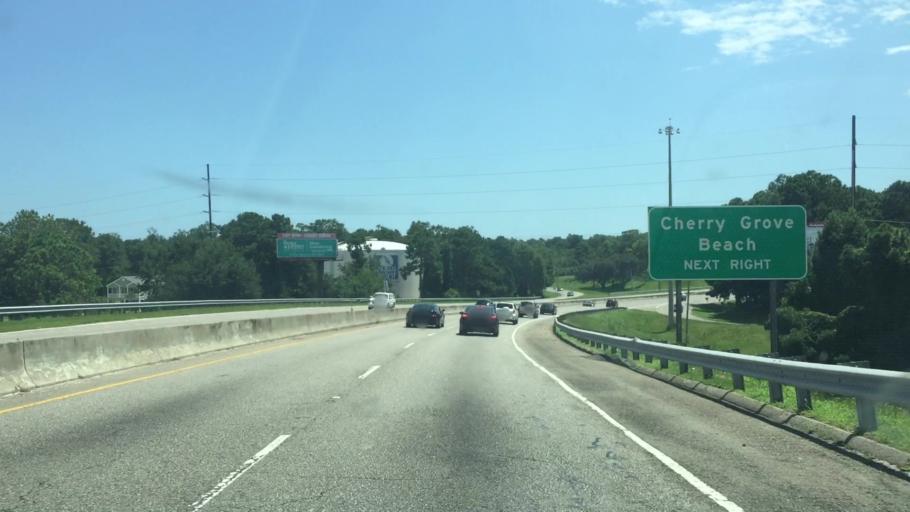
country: US
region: South Carolina
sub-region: Horry County
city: North Myrtle Beach
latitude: 33.8506
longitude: -78.6531
